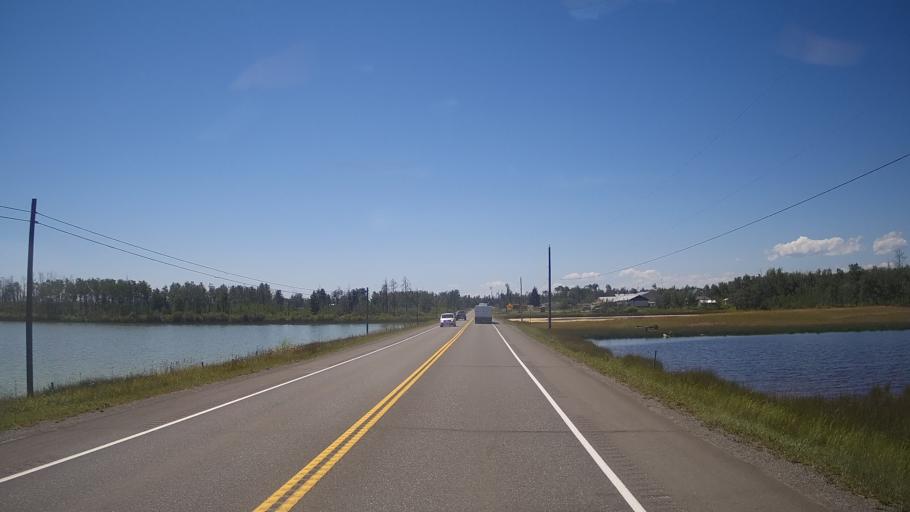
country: CA
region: British Columbia
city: Cache Creek
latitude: 51.3209
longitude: -121.3880
